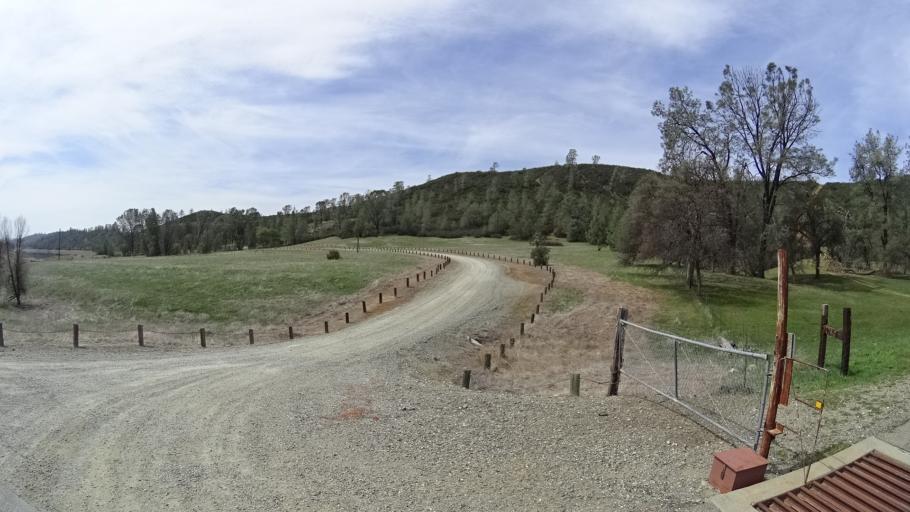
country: US
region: California
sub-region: Glenn County
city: Willows
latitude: 39.5956
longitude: -122.5273
